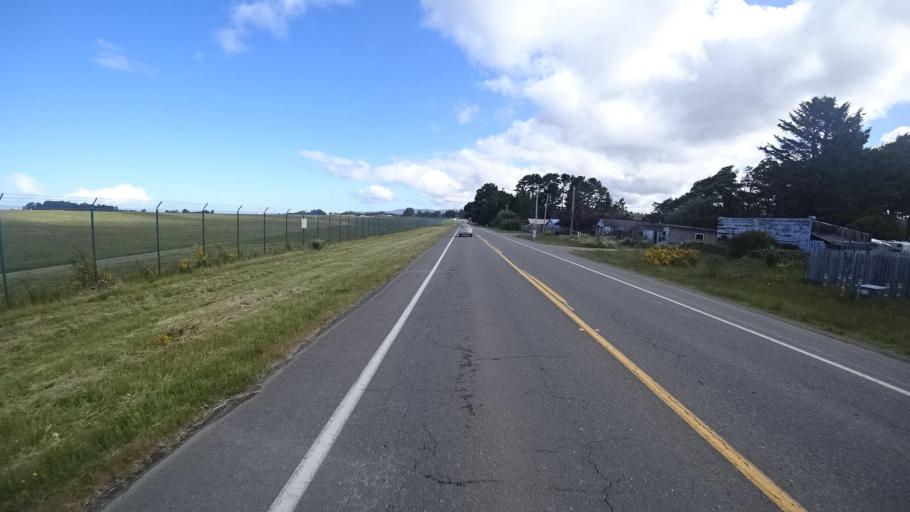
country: US
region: California
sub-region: Humboldt County
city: McKinleyville
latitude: 40.9700
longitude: -124.1007
